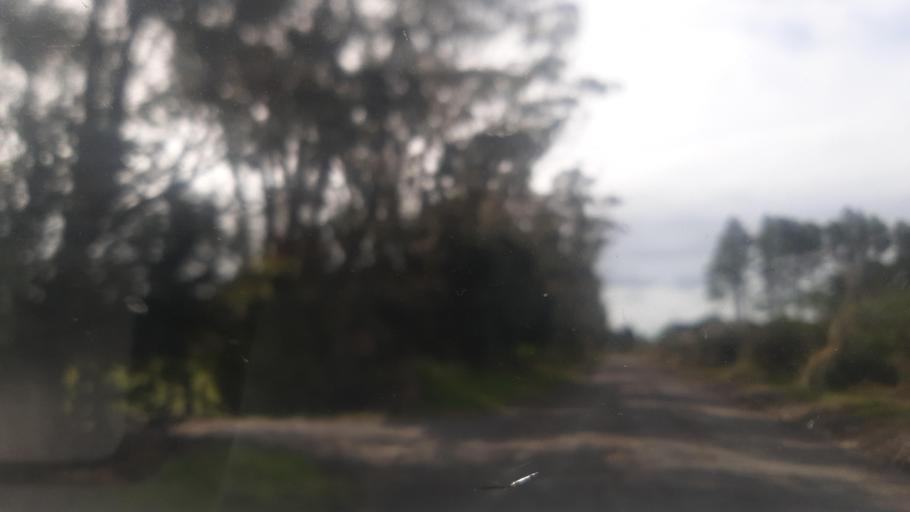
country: NZ
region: Northland
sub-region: Far North District
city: Kaitaia
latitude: -35.0422
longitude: 173.2238
